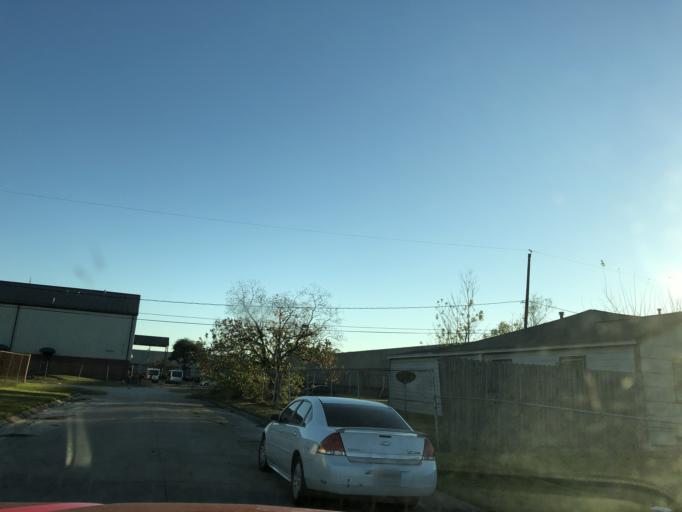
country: US
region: Texas
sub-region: Harris County
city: Jacinto City
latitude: 29.7603
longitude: -95.2666
